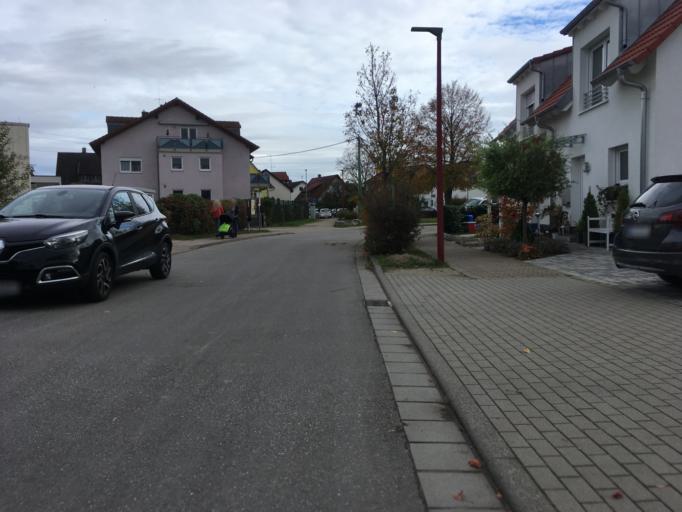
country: DE
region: Baden-Wuerttemberg
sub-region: Freiburg Region
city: Ihringen
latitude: 48.0432
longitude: 7.6436
